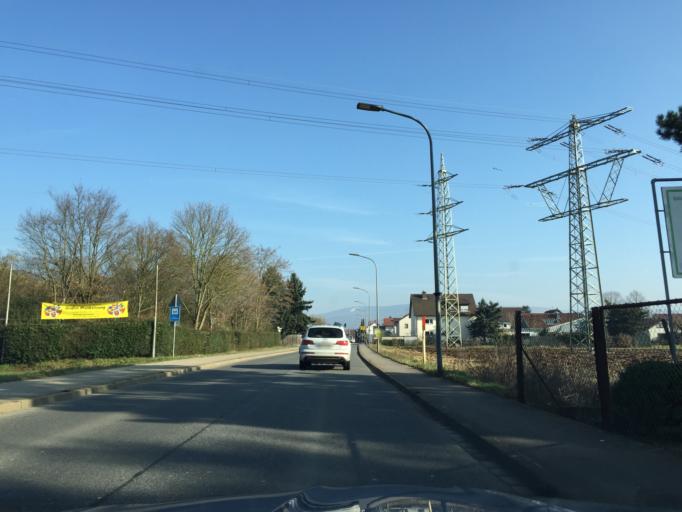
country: DE
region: Baden-Wuerttemberg
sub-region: Karlsruhe Region
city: Eppelheim
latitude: 49.3989
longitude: 8.6202
